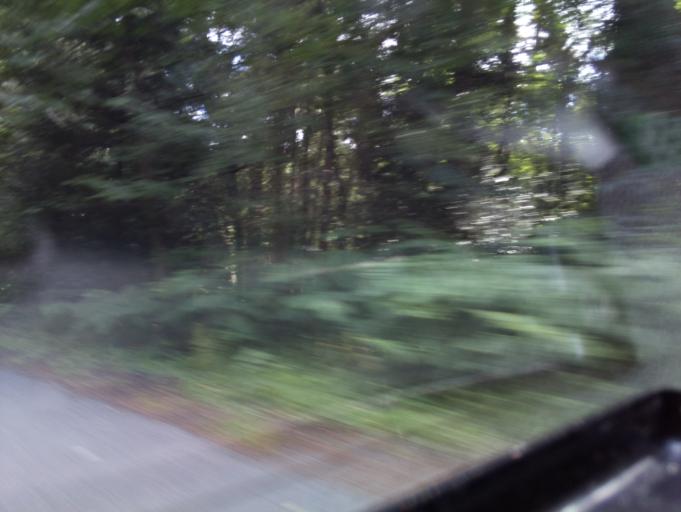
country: GB
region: England
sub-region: Gloucestershire
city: Cinderford
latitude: 51.7978
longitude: -2.4936
